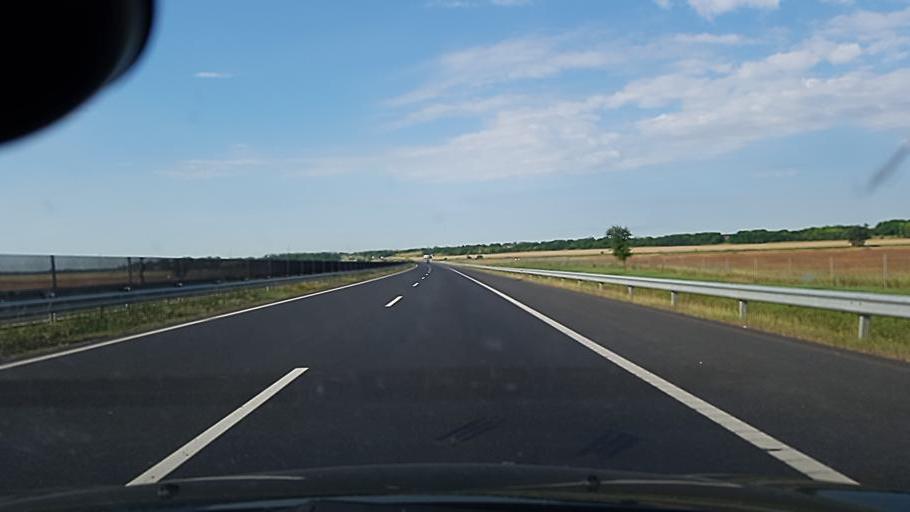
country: HU
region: Fejer
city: Rackeresztur
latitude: 47.2311
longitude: 18.8221
